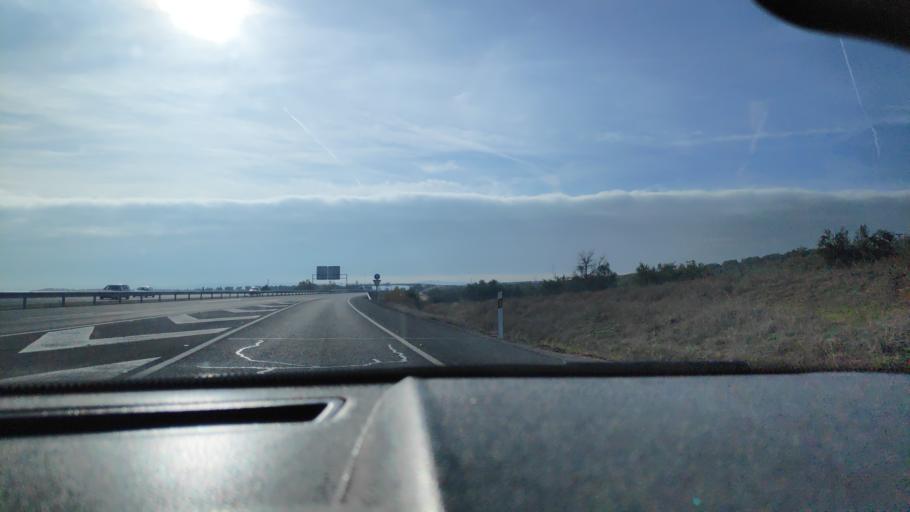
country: ES
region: Andalusia
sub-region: Provincia de Jaen
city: Bailen
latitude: 38.0962
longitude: -3.7401
